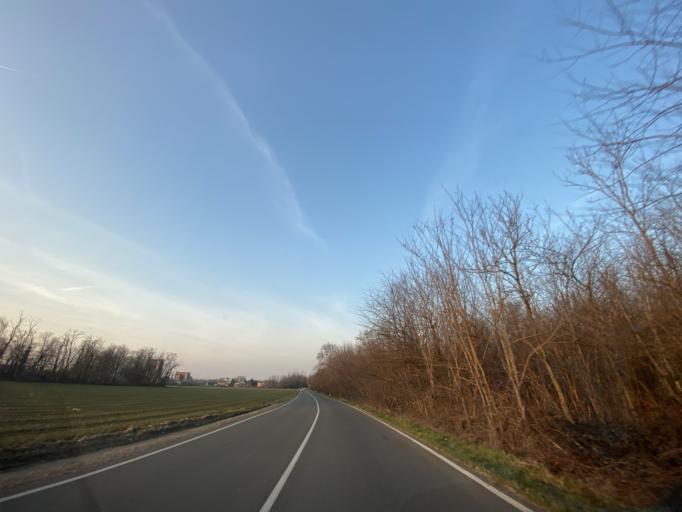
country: IT
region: Lombardy
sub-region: Citta metropolitana di Milano
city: Garbagnate Milanese
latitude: 45.5826
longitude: 9.0631
